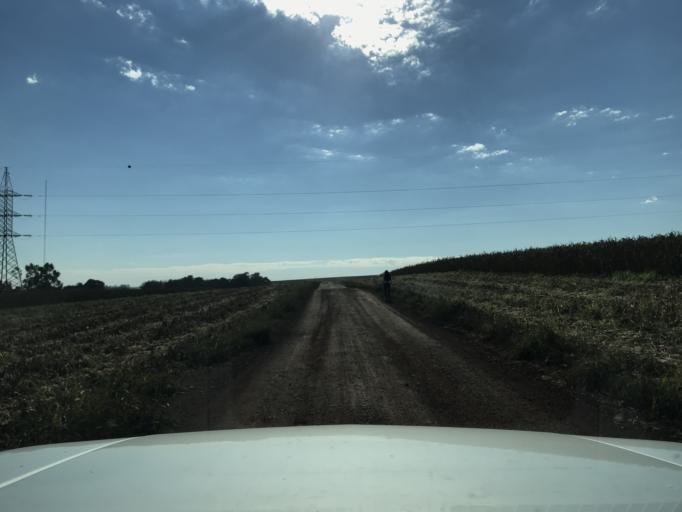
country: BR
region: Parana
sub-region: Palotina
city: Palotina
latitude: -24.2730
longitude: -53.8178
